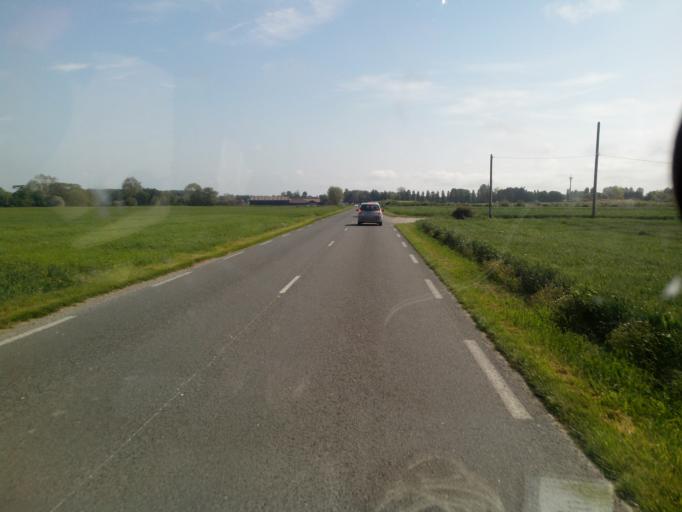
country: FR
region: Picardie
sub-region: Departement de la Somme
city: Quend
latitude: 50.3252
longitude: 1.6406
